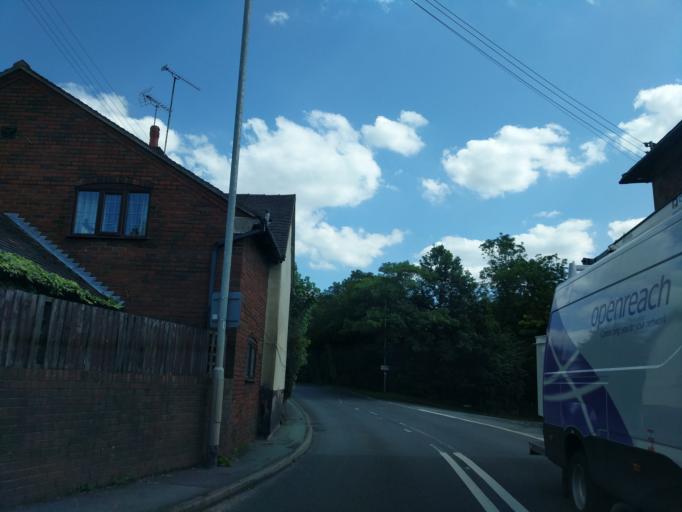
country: GB
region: England
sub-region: Staffordshire
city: Cheadle
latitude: 52.9444
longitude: -1.9765
